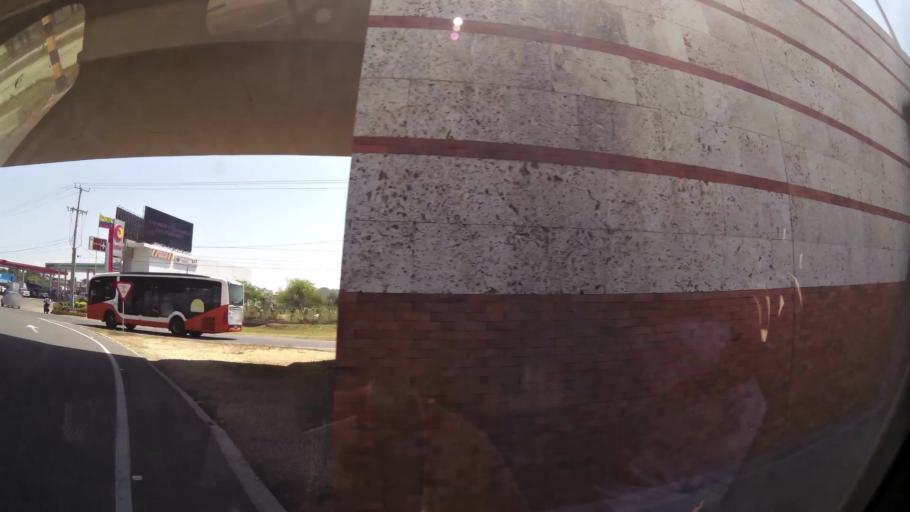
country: CO
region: Bolivar
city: Cartagena
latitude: 10.4408
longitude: -75.5285
